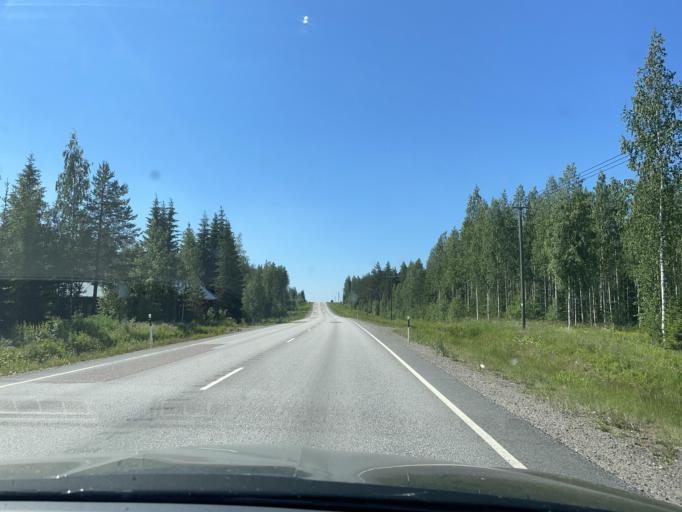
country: FI
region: Central Finland
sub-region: Saarijaervi-Viitasaari
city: Viitasaari
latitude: 63.1482
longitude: 25.8597
